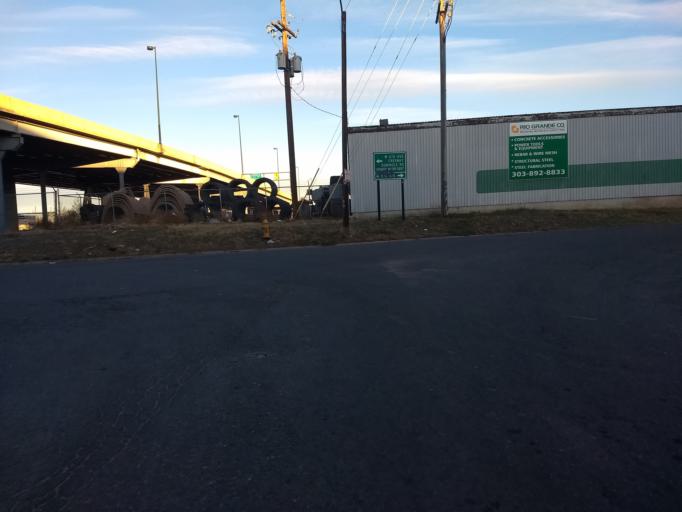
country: US
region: Colorado
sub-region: Denver County
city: Denver
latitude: 39.7254
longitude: -105.0058
